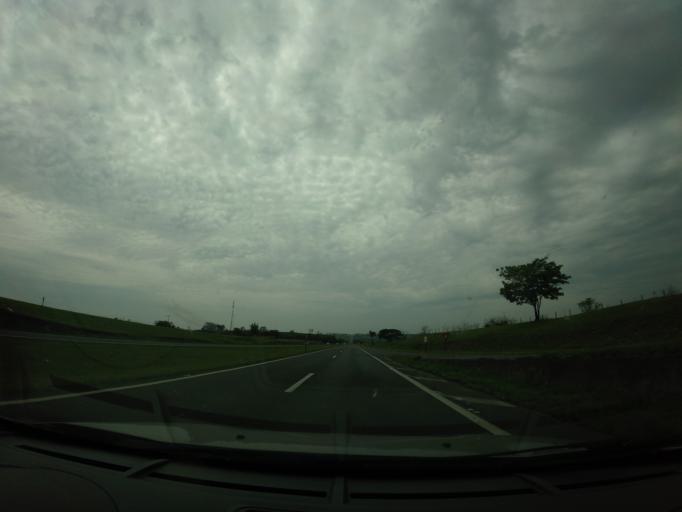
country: BR
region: Sao Paulo
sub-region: Santa Barbara D'Oeste
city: Santa Barbara d'Oeste
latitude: -22.7485
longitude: -47.5031
